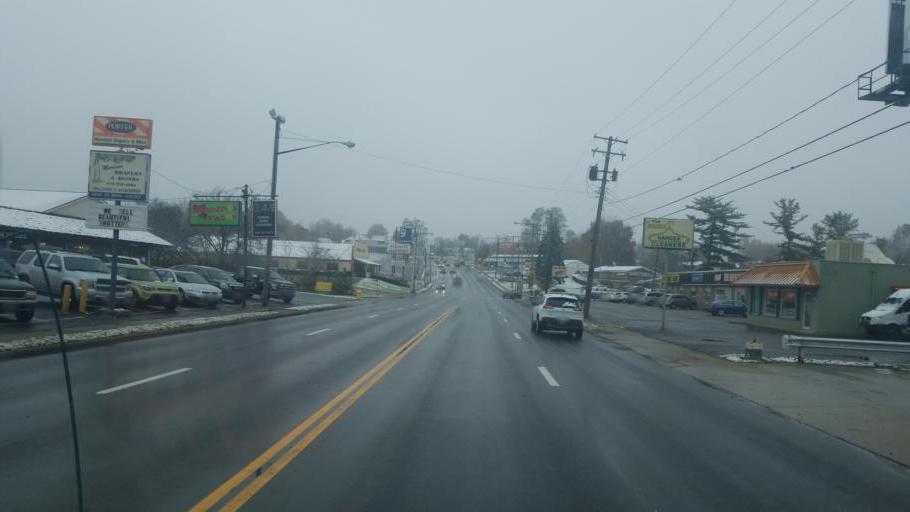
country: US
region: Ohio
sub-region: Richland County
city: Mansfield
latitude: 40.7218
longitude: -82.5431
